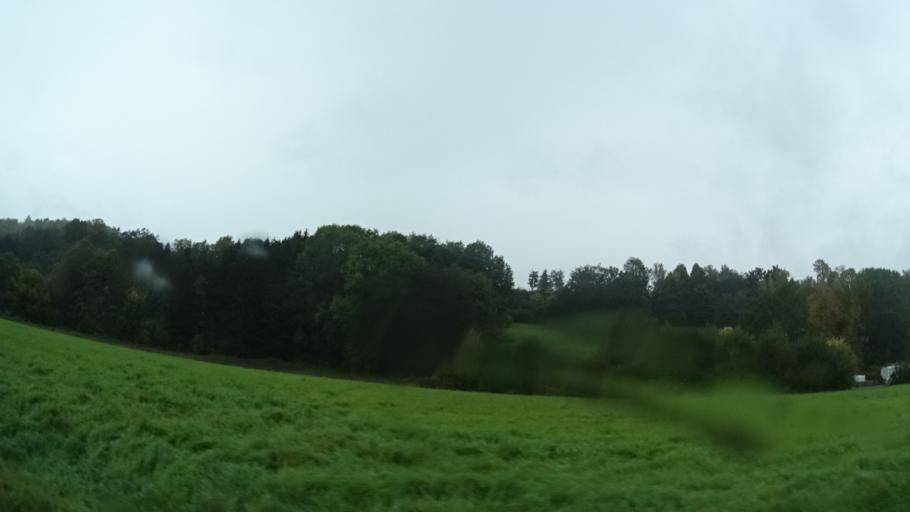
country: DE
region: Bavaria
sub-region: Upper Franconia
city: Kronach
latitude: 50.2500
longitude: 11.3377
